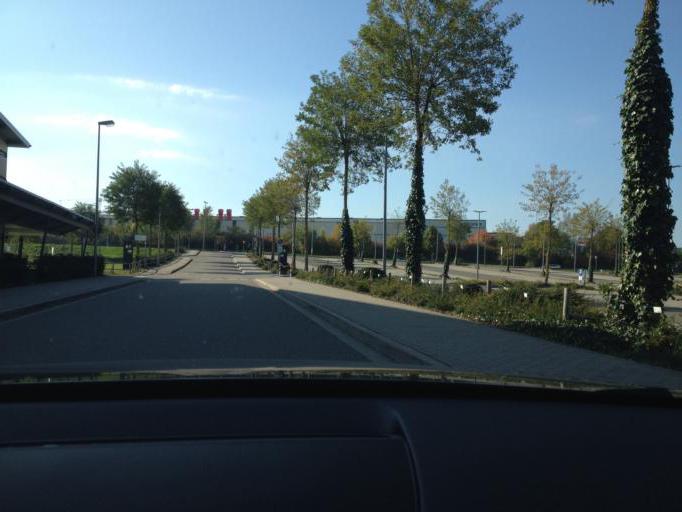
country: DE
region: Rheinland-Pfalz
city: Contwig
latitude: 49.2316
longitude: 7.4033
